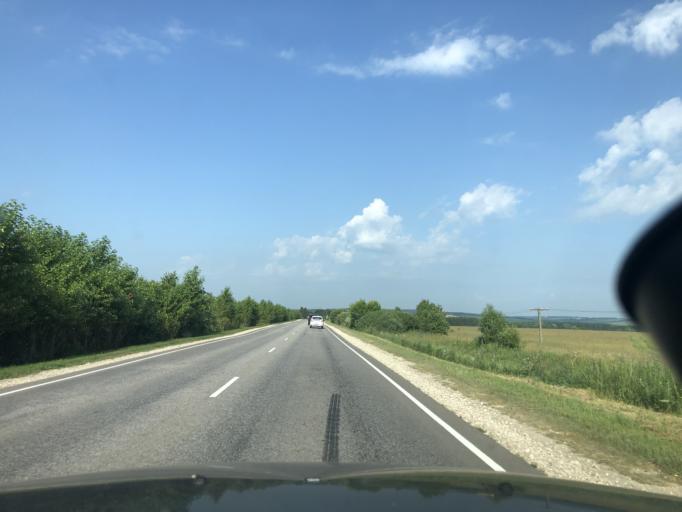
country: RU
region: Tula
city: Krapivna
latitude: 54.1142
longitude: 37.1660
